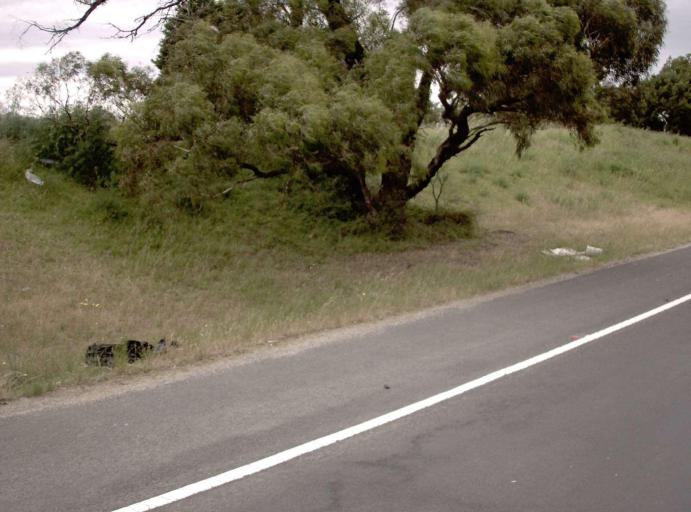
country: AU
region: Victoria
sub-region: Casey
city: Hampton Park
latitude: -38.0385
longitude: 145.2495
